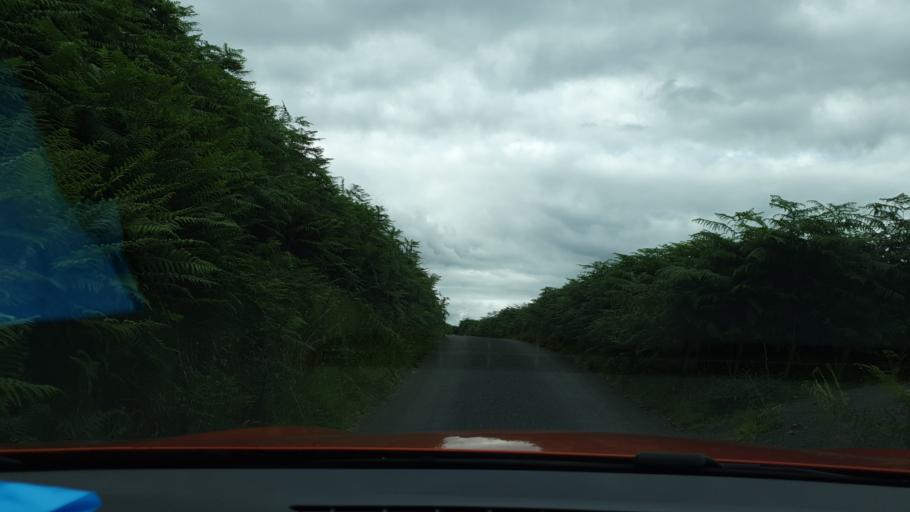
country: GB
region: England
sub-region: Cumbria
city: Ambleside
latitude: 54.5637
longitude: -2.8803
